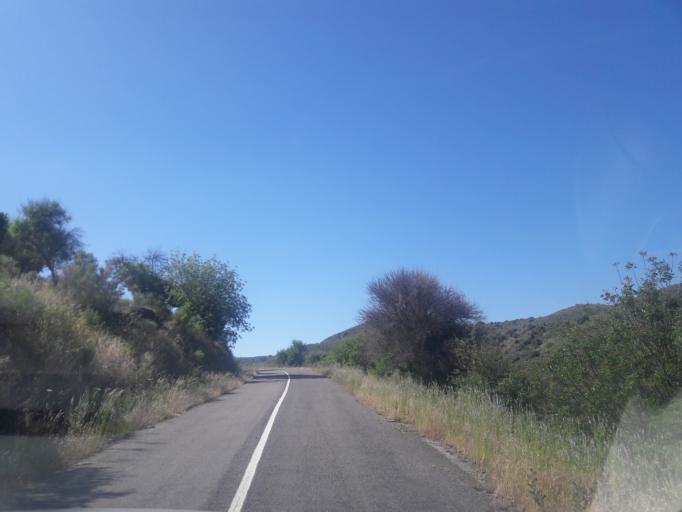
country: ES
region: Castille and Leon
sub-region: Provincia de Salamanca
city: Saucelle
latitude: 41.0200
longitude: -6.7510
